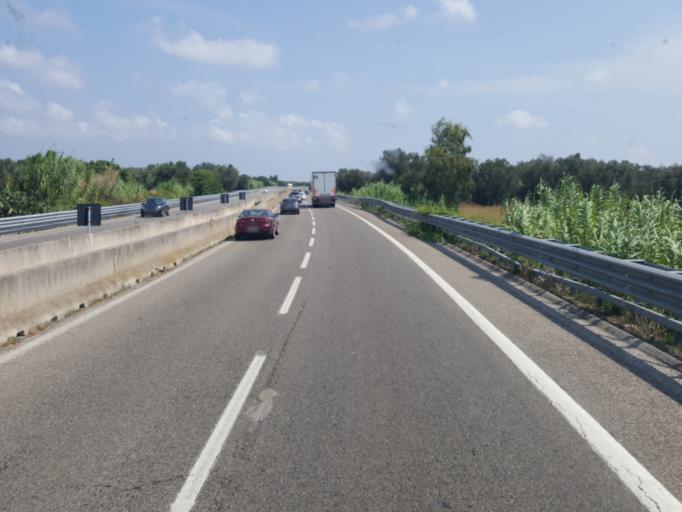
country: IT
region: Apulia
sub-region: Provincia di Brindisi
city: Torchiarolo
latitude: 40.5037
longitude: 18.0262
